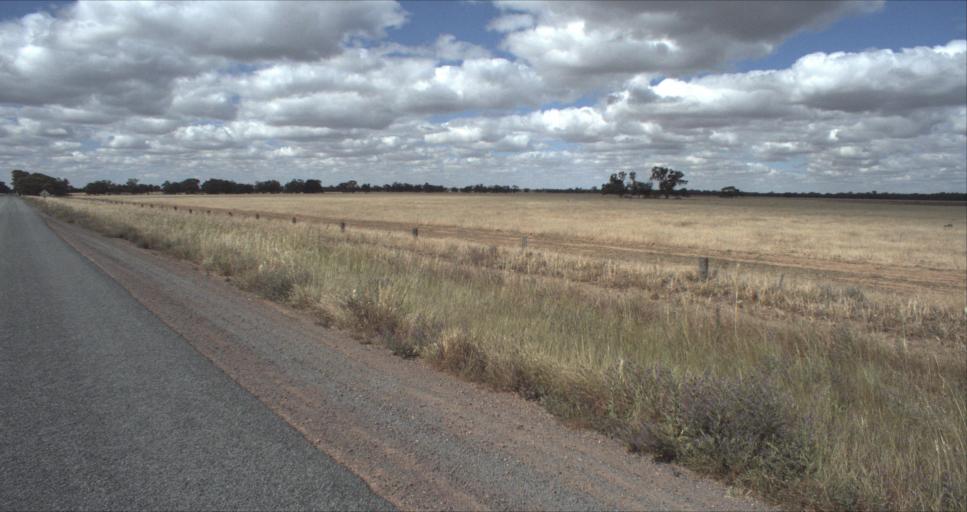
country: AU
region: New South Wales
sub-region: Leeton
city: Leeton
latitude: -34.6965
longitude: 146.3427
